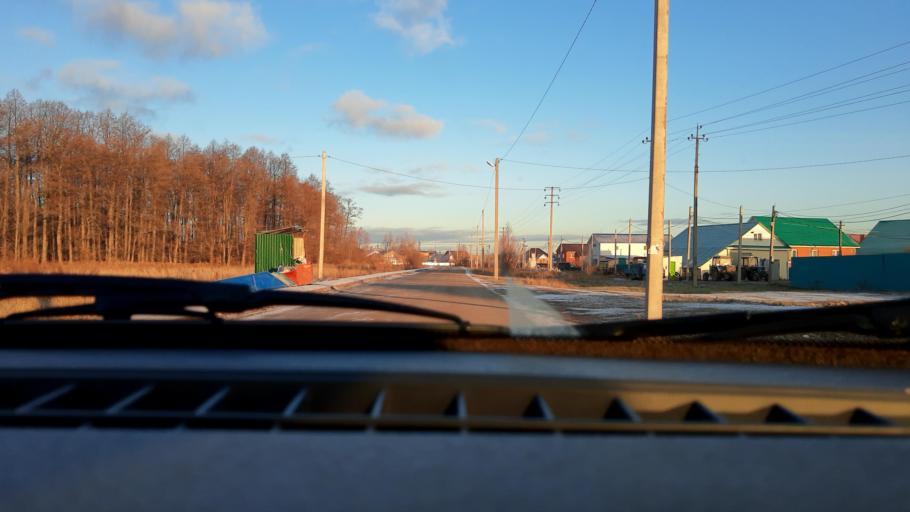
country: RU
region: Bashkortostan
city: Mikhaylovka
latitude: 54.7817
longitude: 55.8218
